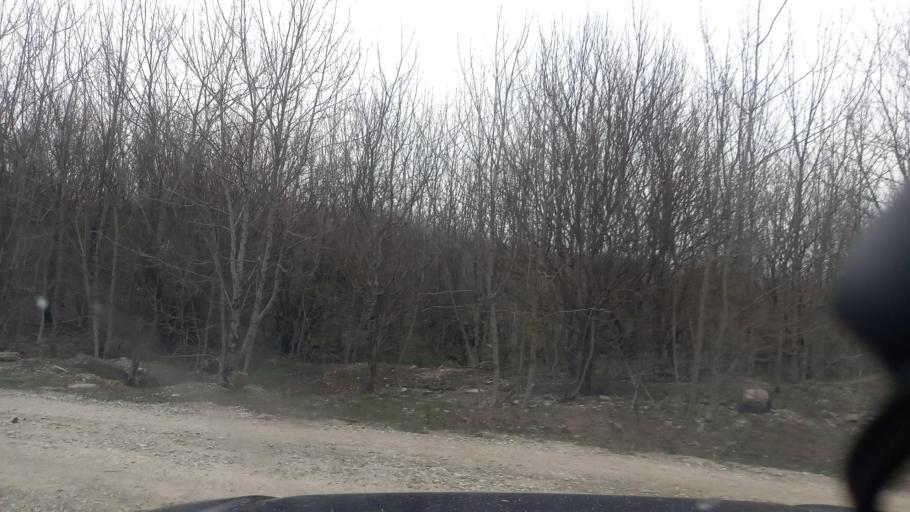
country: RU
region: Krasnodarskiy
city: Divnomorskoye
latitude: 44.6029
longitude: 38.2774
